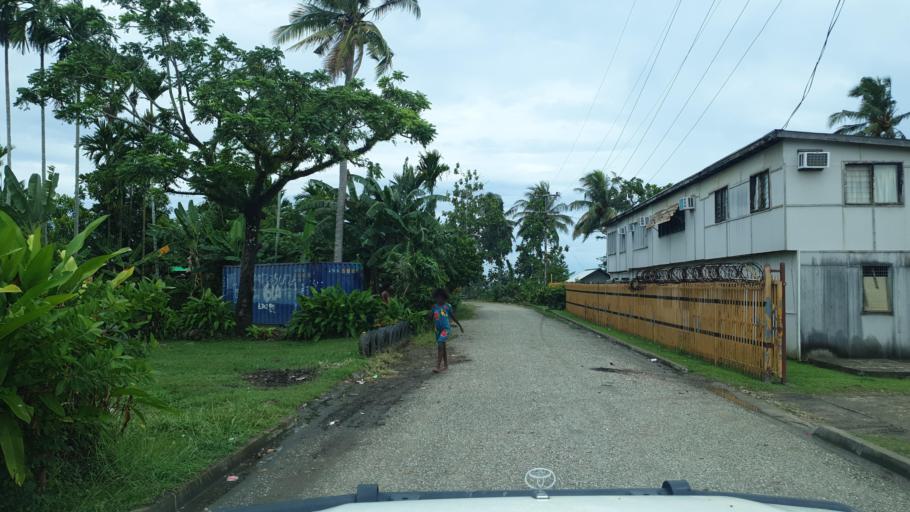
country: PG
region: Gulf
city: Kerema
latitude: -7.9608
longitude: 145.7716
